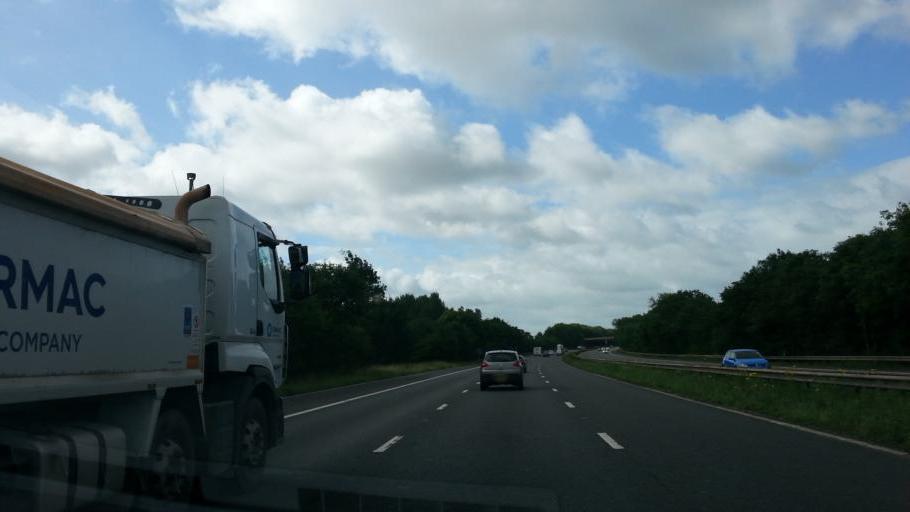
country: GB
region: England
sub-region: Leicestershire
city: Hinckley
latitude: 52.4944
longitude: -1.3851
